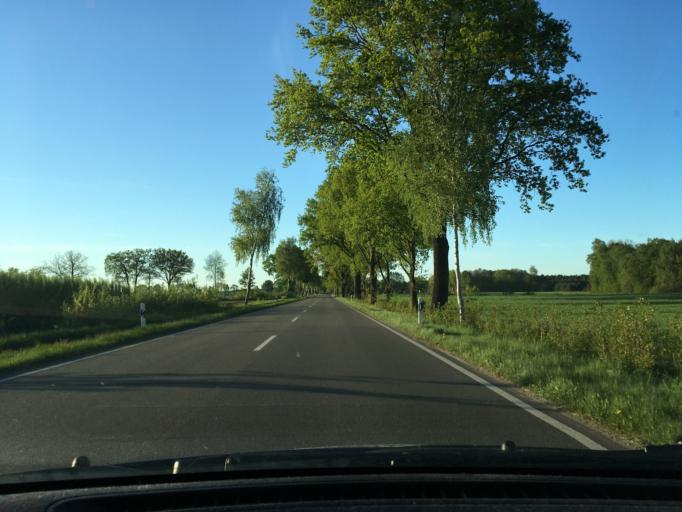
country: DE
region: Lower Saxony
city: Oldendorf
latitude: 53.1721
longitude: 10.2109
